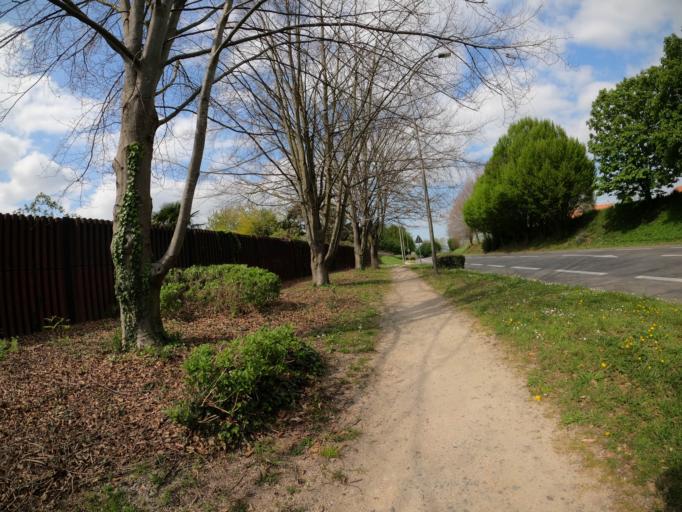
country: FR
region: Aquitaine
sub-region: Departement des Pyrenees-Atlantiques
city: Lons
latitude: 43.3369
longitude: -0.3852
